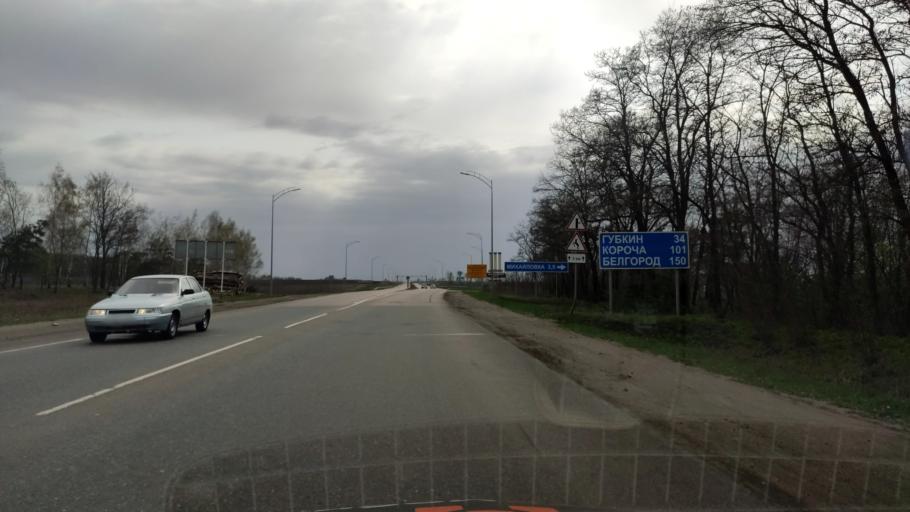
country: RU
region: Belgorod
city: Staryy Oskol
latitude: 51.4290
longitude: 37.8982
